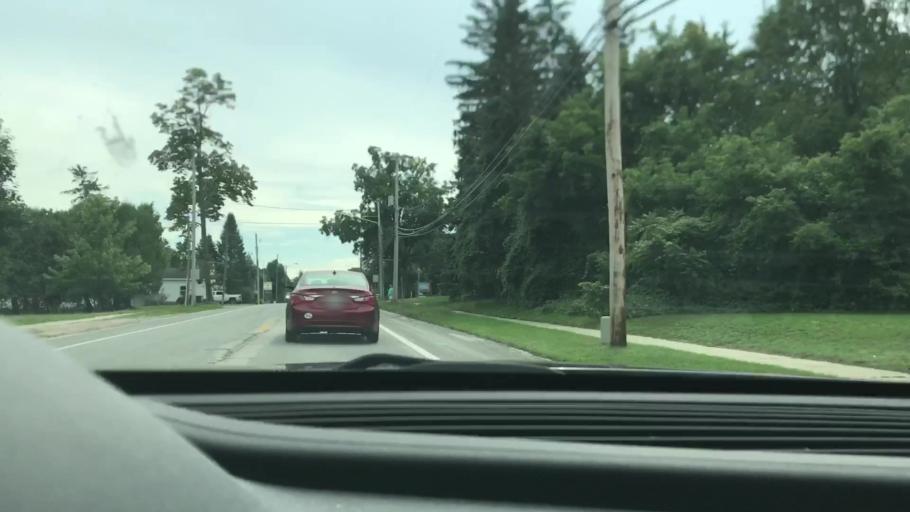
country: US
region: Michigan
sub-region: Antrim County
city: Bellaire
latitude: 45.0737
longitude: -85.2641
